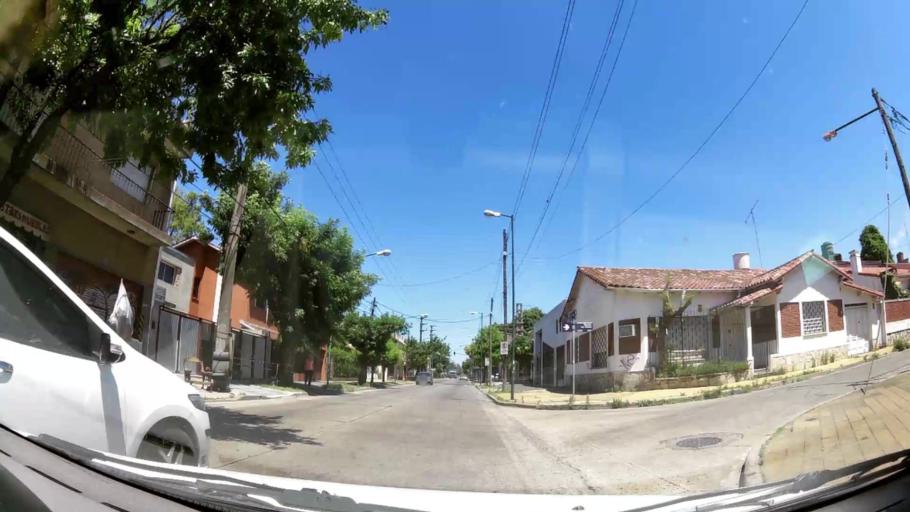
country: AR
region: Buenos Aires
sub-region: Partido de Vicente Lopez
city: Olivos
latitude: -34.5036
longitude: -58.5104
